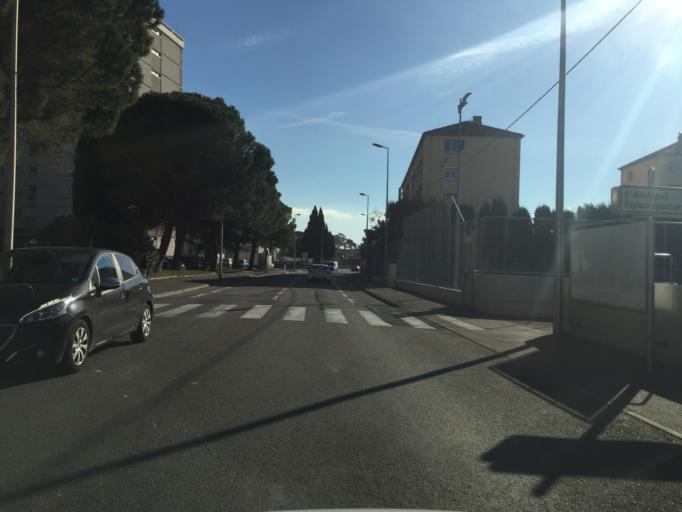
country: FR
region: Provence-Alpes-Cote d'Azur
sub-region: Departement des Bouches-du-Rhone
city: Salon-de-Provence
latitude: 43.6492
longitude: 5.1016
